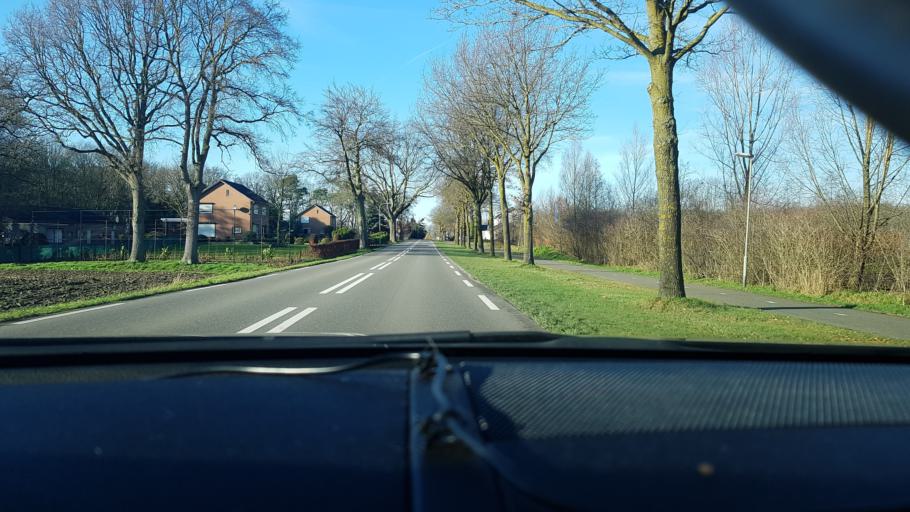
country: NL
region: Limburg
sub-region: Gemeente Beesel
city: Beesel
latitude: 51.2969
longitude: 6.0396
